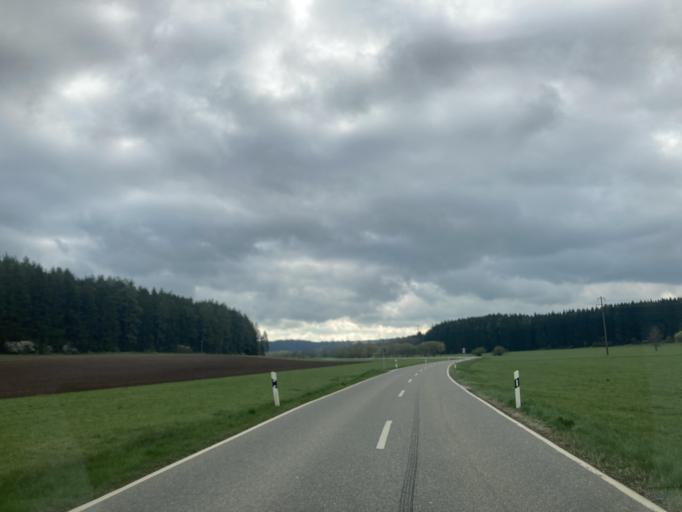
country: DE
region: Baden-Wuerttemberg
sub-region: Freiburg Region
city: Villingen-Schwenningen
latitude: 48.0321
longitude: 8.4347
